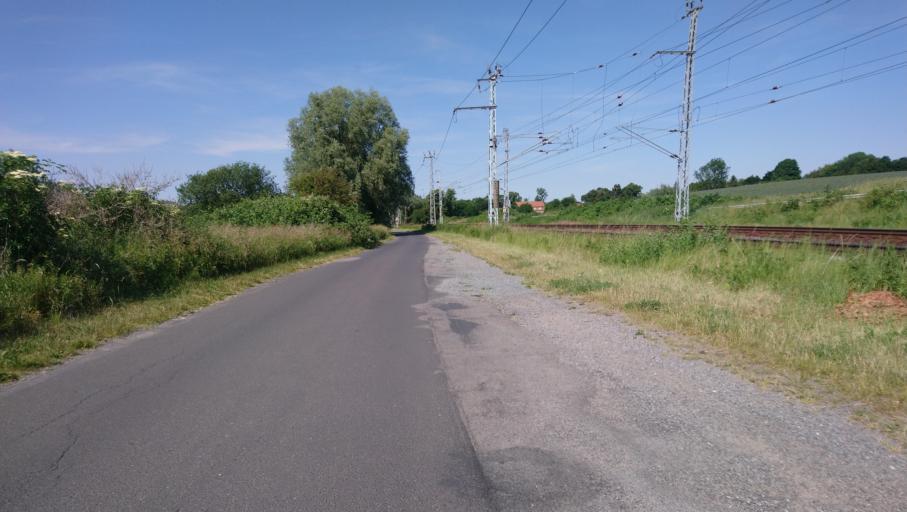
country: DE
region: Mecklenburg-Vorpommern
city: Dierkow-Neu
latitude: 54.0894
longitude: 12.1787
